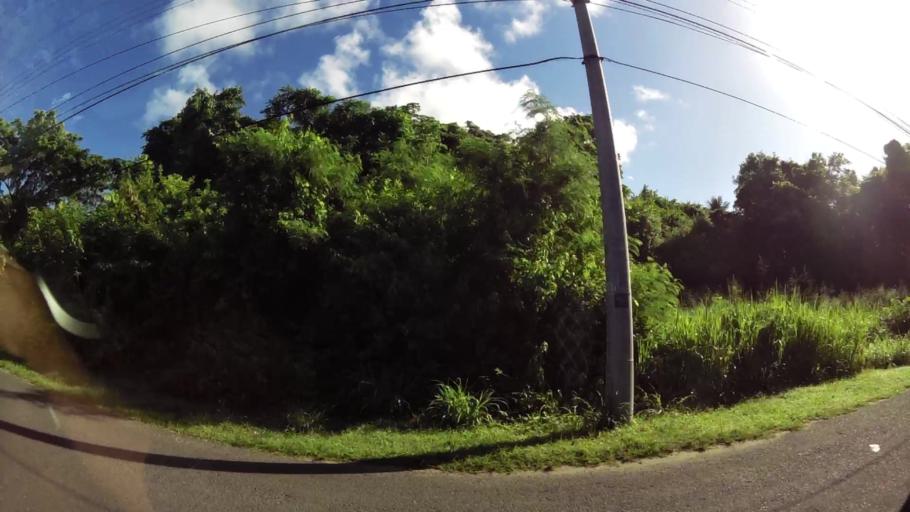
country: TT
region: Tobago
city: Scarborough
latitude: 11.1609
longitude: -60.8393
